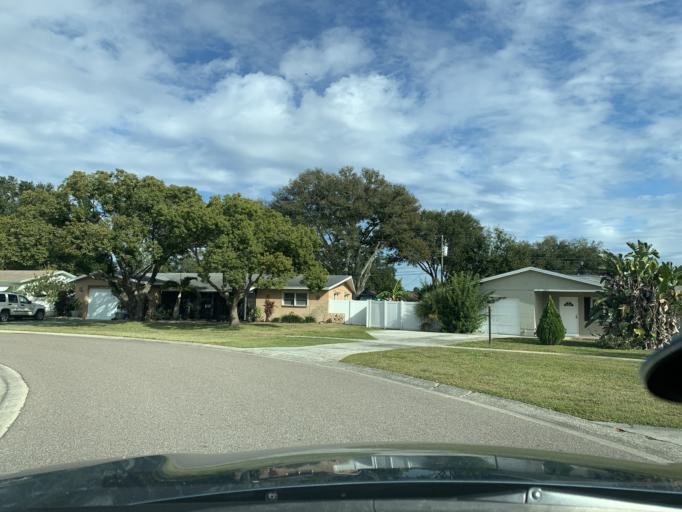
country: US
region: Florida
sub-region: Pinellas County
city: Kenneth City
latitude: 27.8049
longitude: -82.7354
